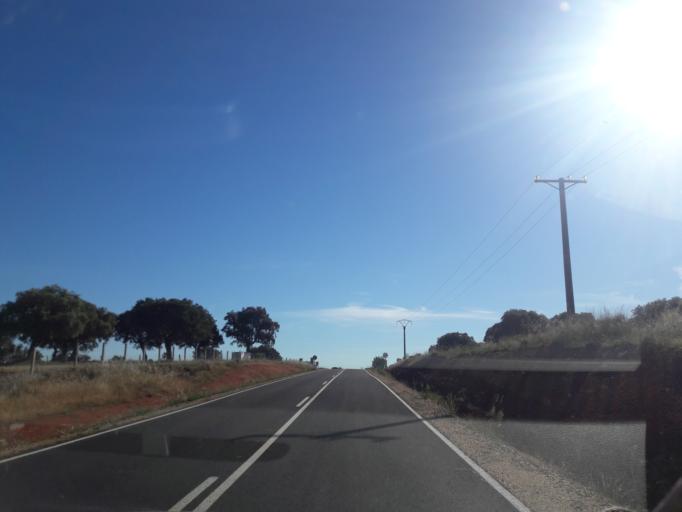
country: ES
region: Castille and Leon
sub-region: Provincia de Salamanca
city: Calzada de Don Diego
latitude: 40.8539
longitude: -5.8660
